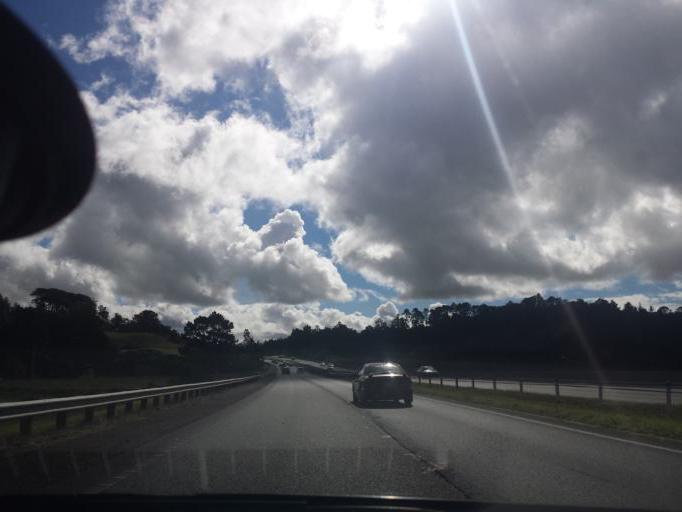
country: NZ
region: Auckland
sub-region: Auckland
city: Rothesay Bay
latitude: -36.6845
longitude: 174.6999
